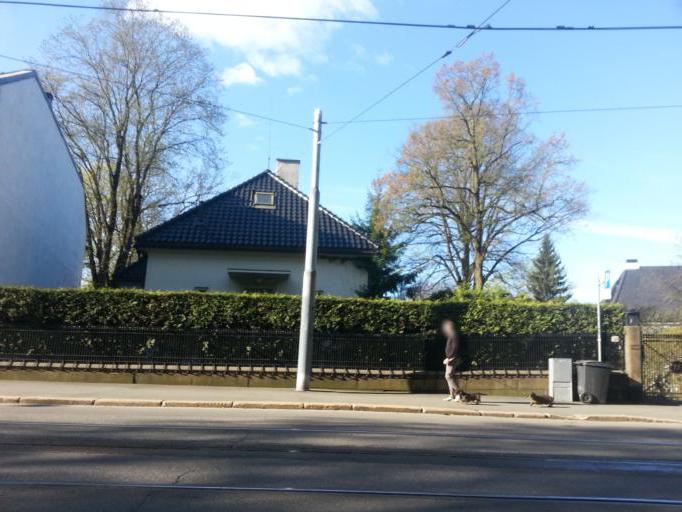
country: NO
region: Oslo
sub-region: Oslo
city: Sjolyststranda
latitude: 59.9136
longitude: 10.7036
